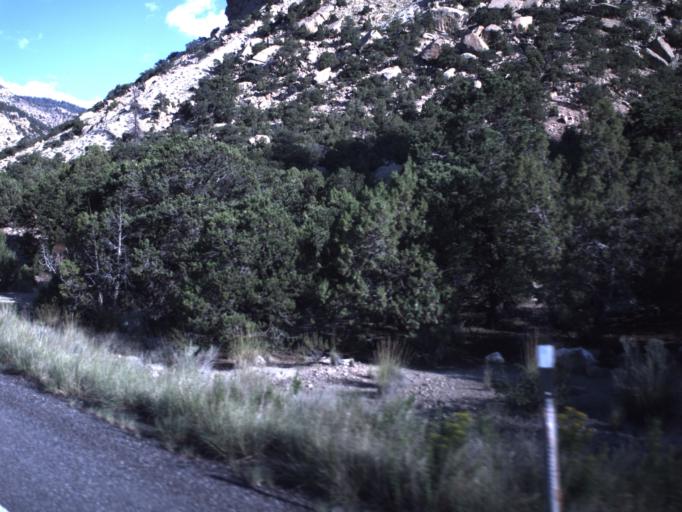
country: US
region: Utah
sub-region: Emery County
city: Huntington
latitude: 39.3931
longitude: -111.0978
